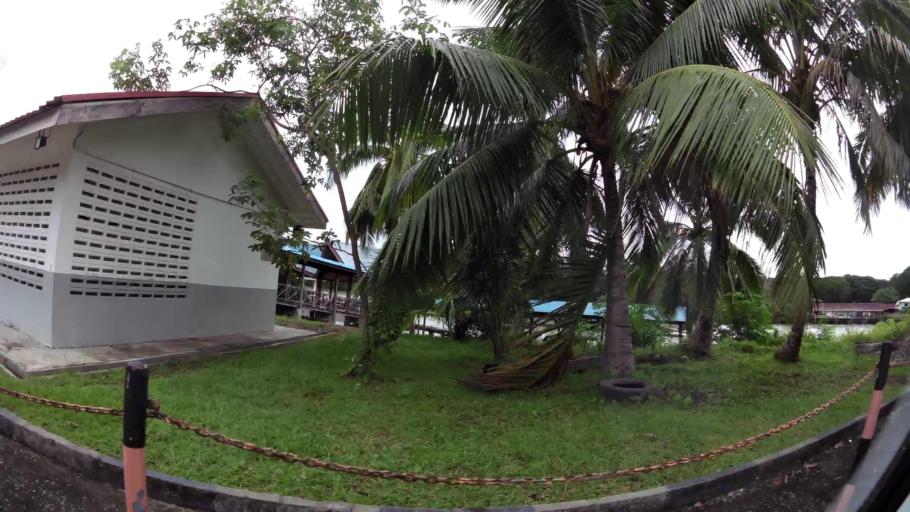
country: BN
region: Brunei and Muara
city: Bandar Seri Begawan
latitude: 4.8948
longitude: 114.9342
